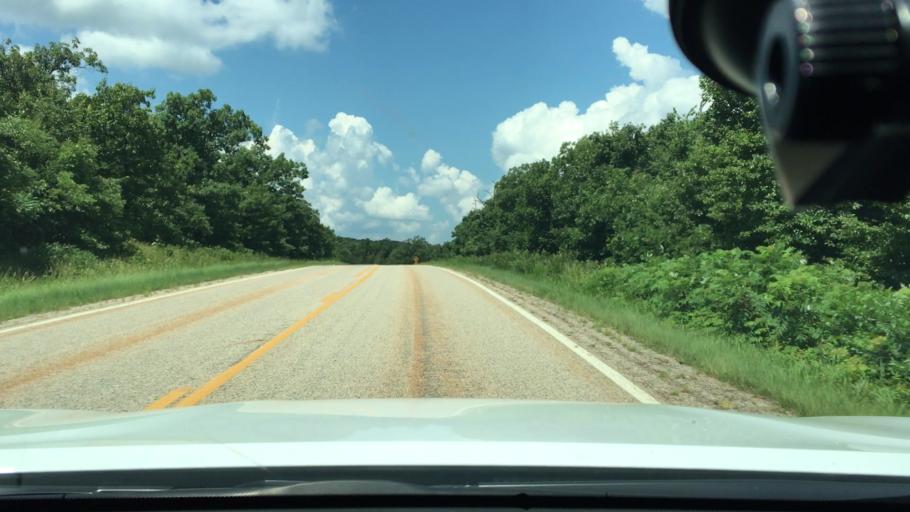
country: US
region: Arkansas
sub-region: Logan County
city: Paris
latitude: 35.1768
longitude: -93.6114
